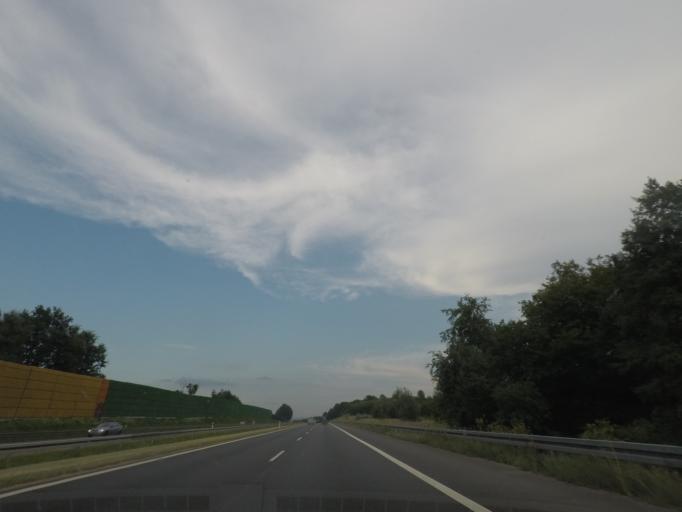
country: PL
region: Lesser Poland Voivodeship
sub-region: Powiat krakowski
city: Czulow
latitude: 50.0813
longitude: 19.7053
